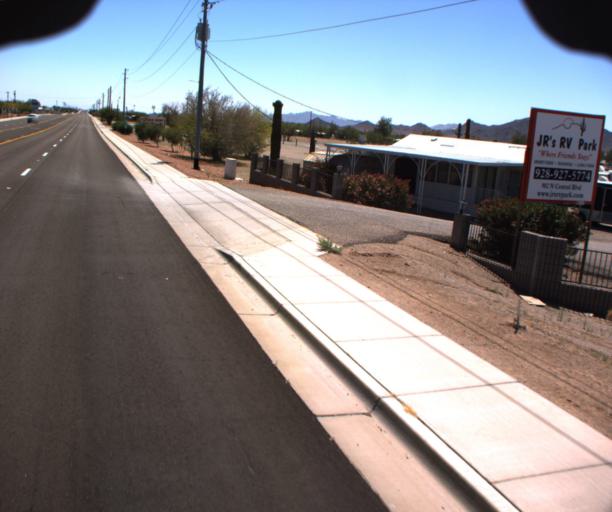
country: US
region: Arizona
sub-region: La Paz County
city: Quartzsite
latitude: 33.6812
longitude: -114.2171
